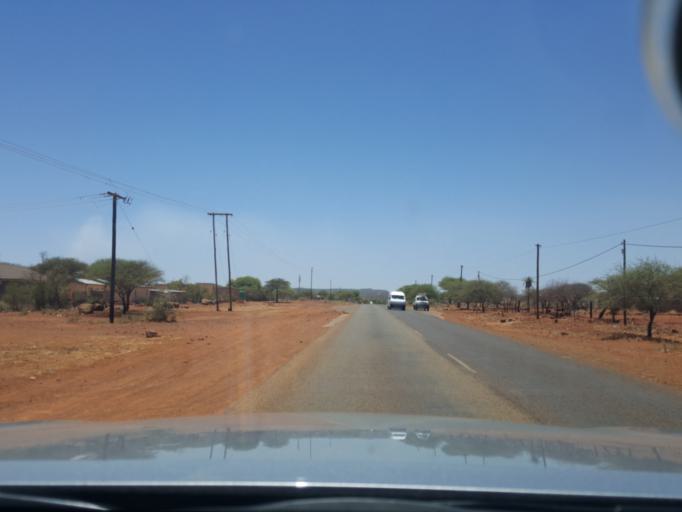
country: ZA
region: North-West
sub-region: Ngaka Modiri Molema District Municipality
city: Zeerust
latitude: -25.4232
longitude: 25.9557
